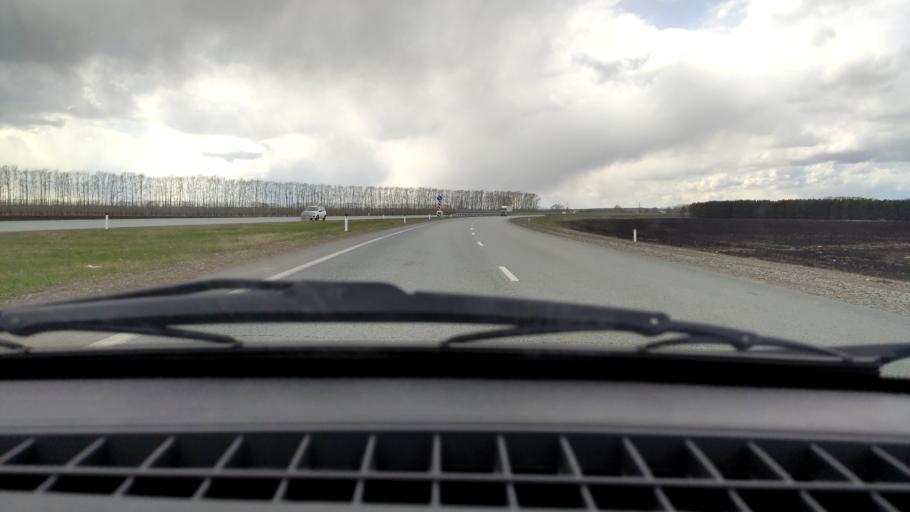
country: RU
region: Bashkortostan
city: Asanovo
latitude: 54.9818
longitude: 55.5357
